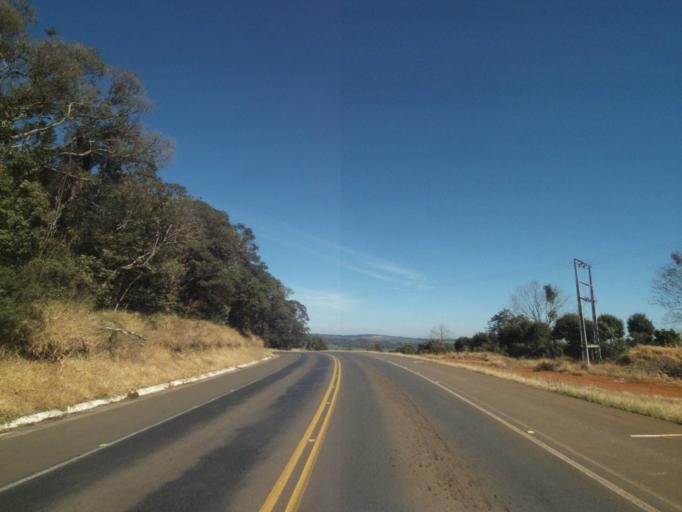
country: BR
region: Parana
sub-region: Tibagi
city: Tibagi
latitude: -24.6959
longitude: -50.4447
